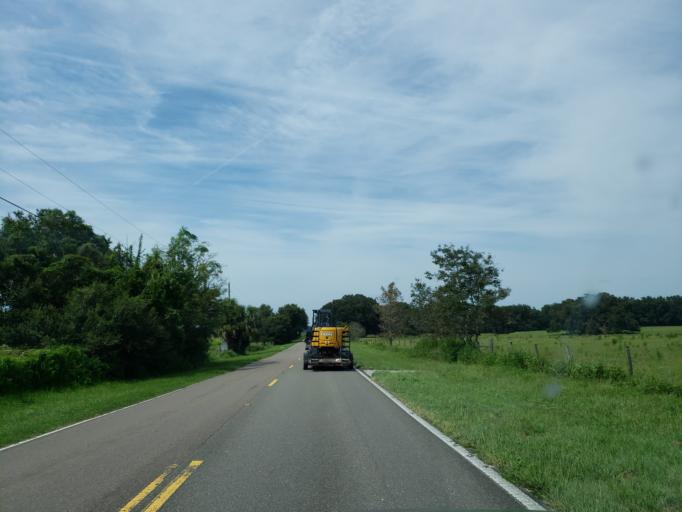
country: US
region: Florida
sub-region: Pasco County
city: San Antonio
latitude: 28.3085
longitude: -82.2786
